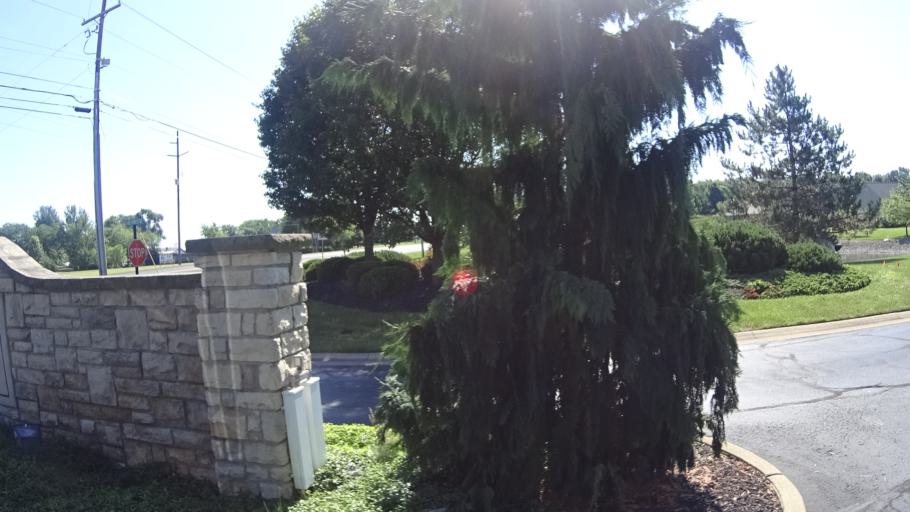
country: US
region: Ohio
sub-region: Erie County
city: Sandusky
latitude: 41.3958
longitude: -82.6420
